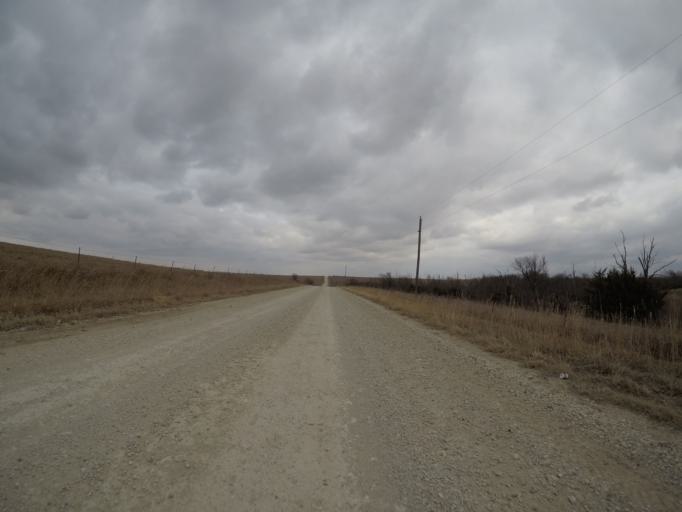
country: US
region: Kansas
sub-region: Morris County
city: Council Grove
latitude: 38.7500
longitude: -96.2795
